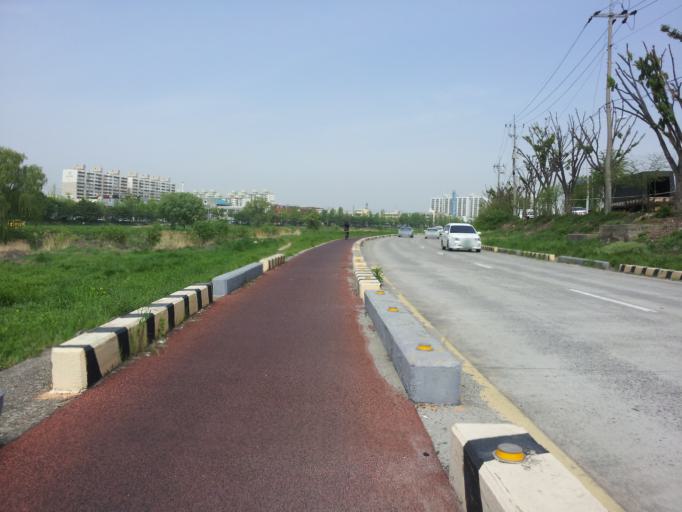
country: KR
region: Daejeon
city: Daejeon
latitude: 36.3396
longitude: 127.4165
